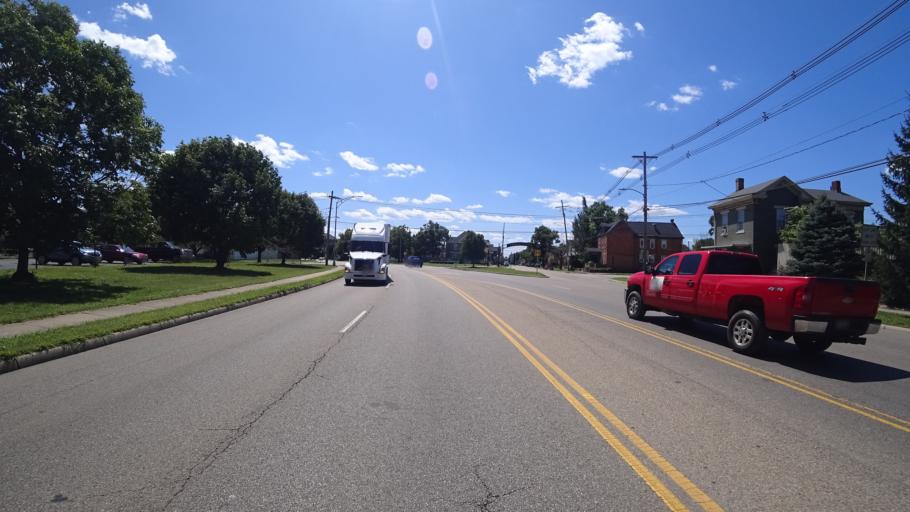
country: US
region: Ohio
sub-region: Butler County
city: Hamilton
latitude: 39.4056
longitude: -84.5572
